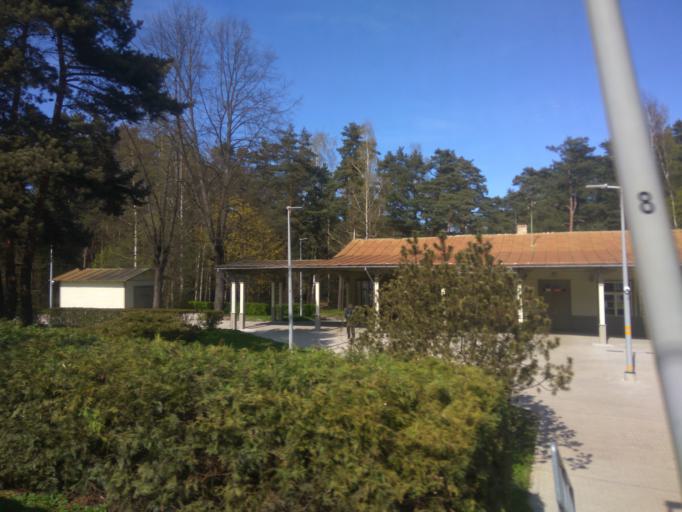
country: LV
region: Babite
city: Pinki
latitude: 56.9822
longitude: 23.8705
